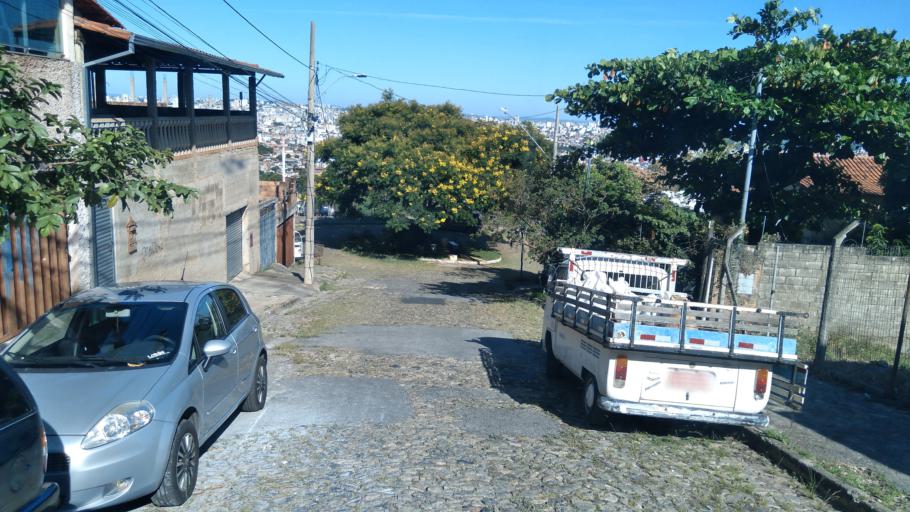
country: BR
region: Minas Gerais
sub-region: Belo Horizonte
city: Belo Horizonte
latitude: -19.9207
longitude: -43.8952
